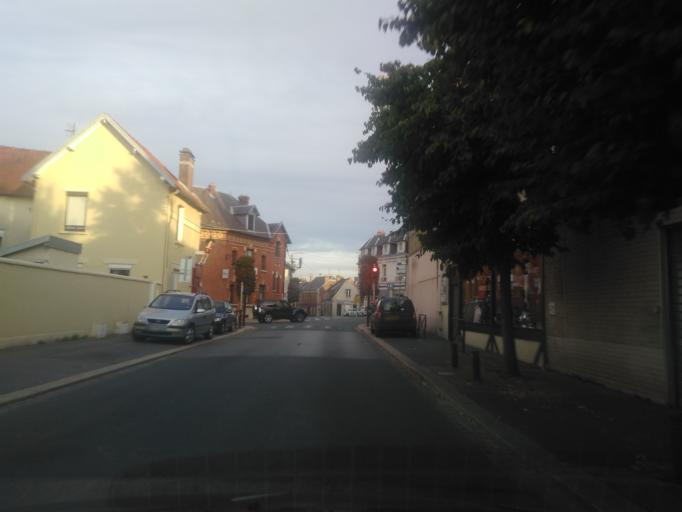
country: FR
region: Picardie
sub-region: Departement de l'Aisne
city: Laon
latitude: 49.5689
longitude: 3.6314
